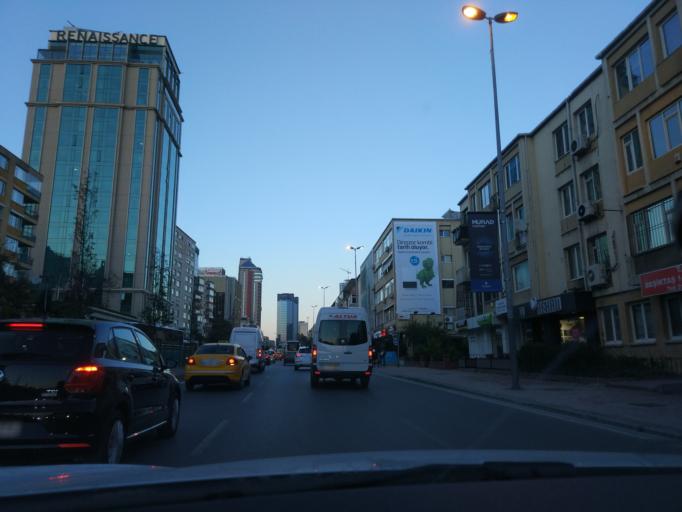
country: TR
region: Istanbul
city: Sisli
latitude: 41.0583
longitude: 29.0104
